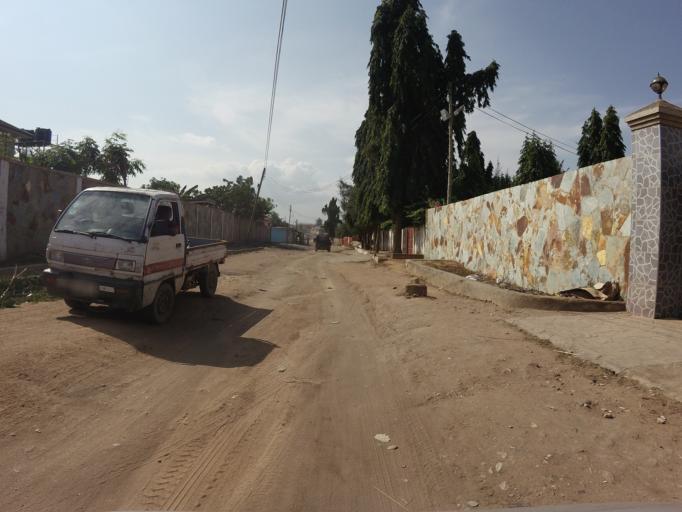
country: GH
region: Greater Accra
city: Dome
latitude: 5.6420
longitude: -0.2346
